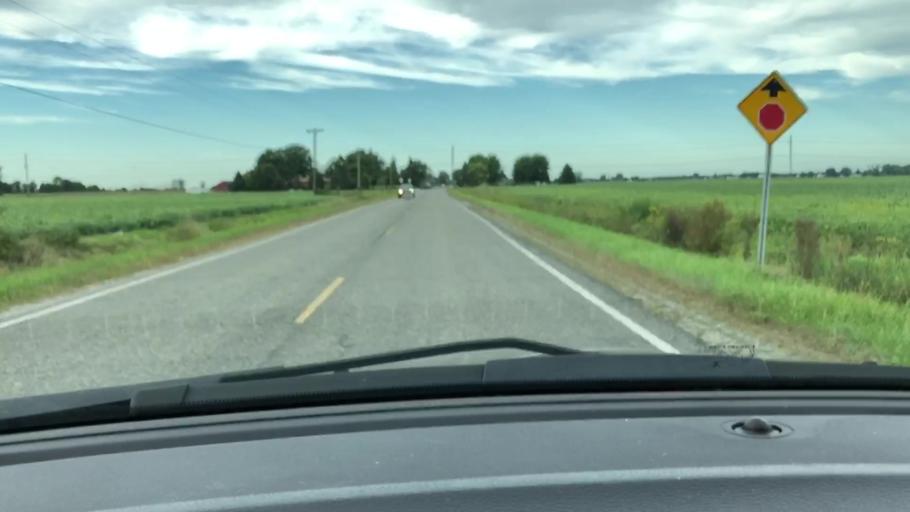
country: US
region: Michigan
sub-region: Saginaw County
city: Zilwaukee
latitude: 43.5051
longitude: -83.9938
